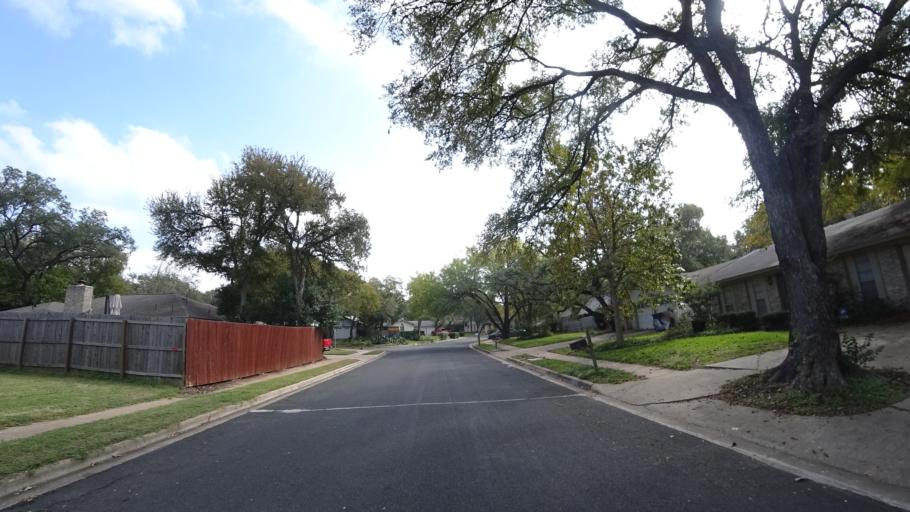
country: US
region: Texas
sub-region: Travis County
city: Shady Hollow
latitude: 30.2028
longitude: -97.8140
